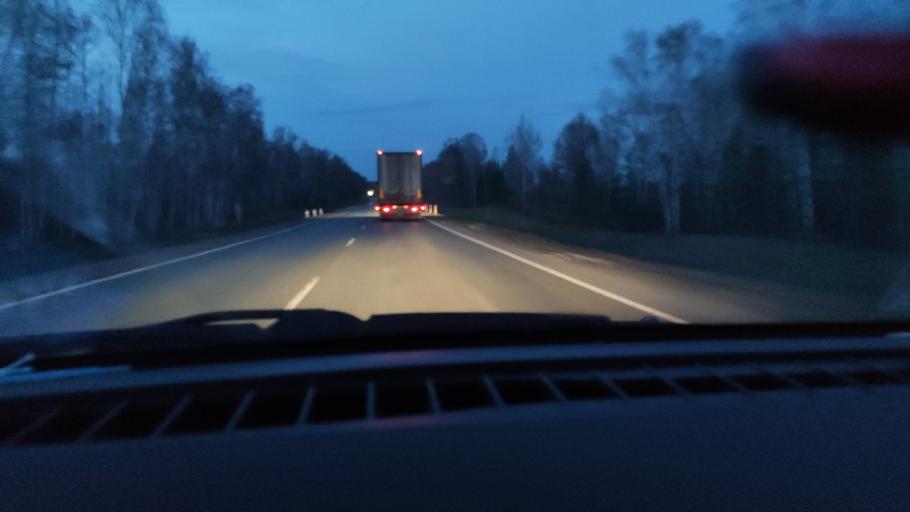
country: RU
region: Saratov
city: Sennoy
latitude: 52.1270
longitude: 46.8554
